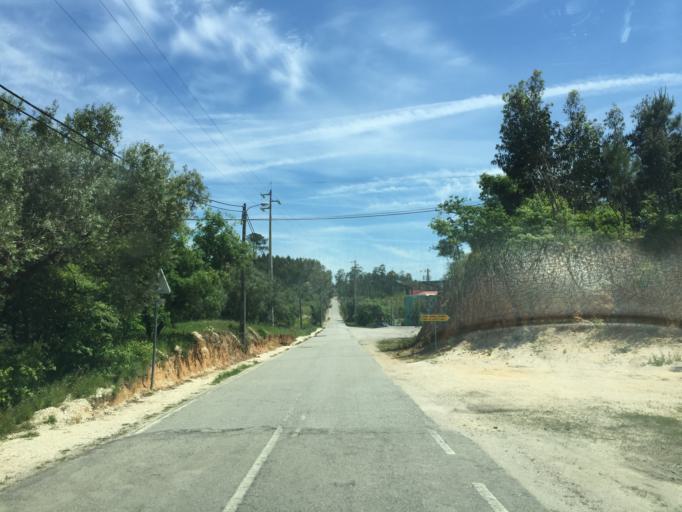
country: PT
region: Leiria
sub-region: Pombal
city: Lourical
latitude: 40.0664
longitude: -8.7276
